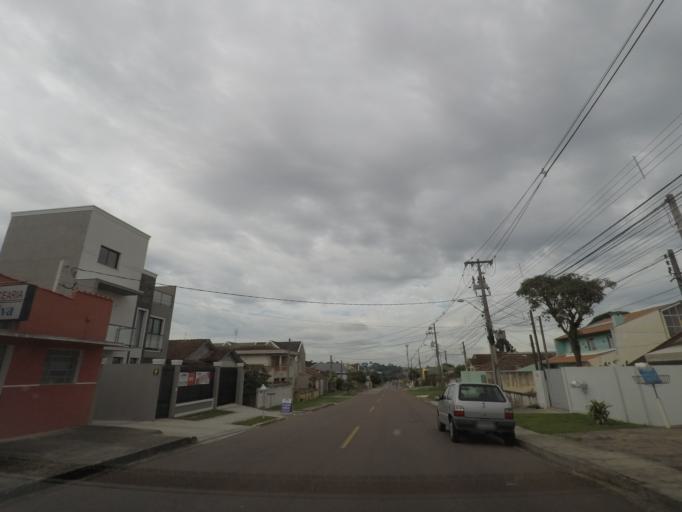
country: BR
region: Parana
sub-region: Pinhais
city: Pinhais
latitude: -25.4701
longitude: -49.2292
